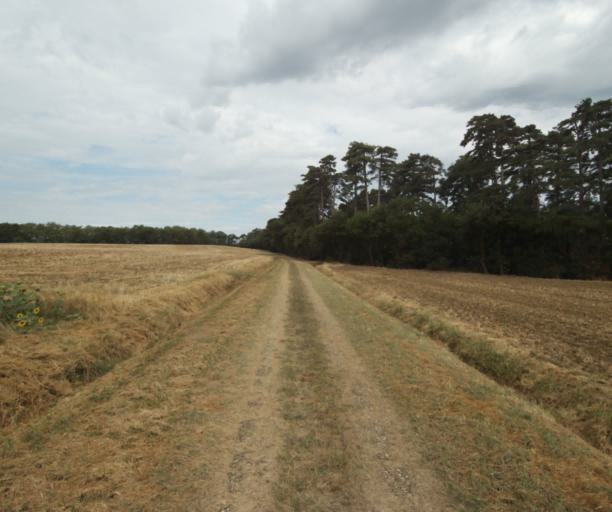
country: FR
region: Midi-Pyrenees
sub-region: Departement de la Haute-Garonne
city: Revel
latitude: 43.4428
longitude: 1.9568
